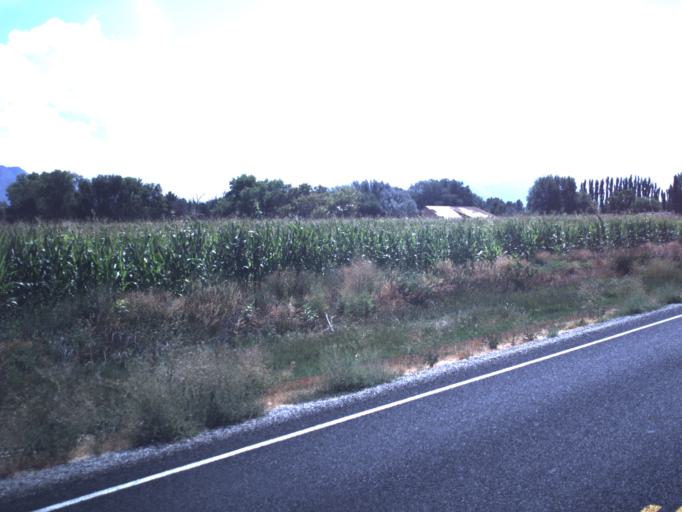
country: US
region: Utah
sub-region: Box Elder County
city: Honeyville
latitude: 41.6239
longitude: -112.1268
